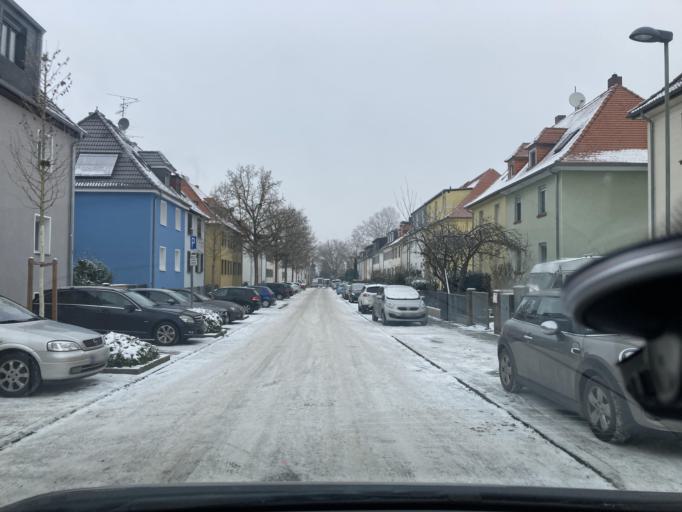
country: DE
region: Hesse
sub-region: Regierungsbezirk Darmstadt
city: Offenbach
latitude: 50.0818
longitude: 8.7820
